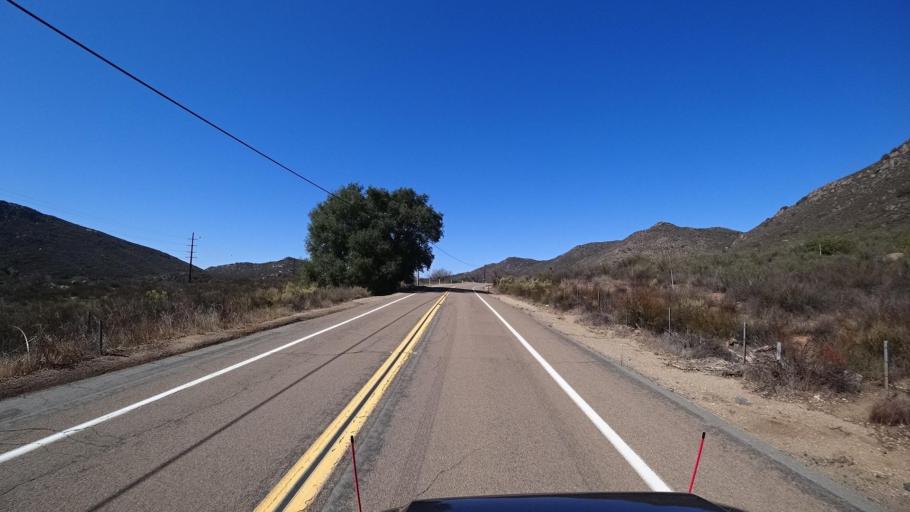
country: US
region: California
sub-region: San Diego County
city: Alpine
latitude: 32.7954
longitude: -116.7446
